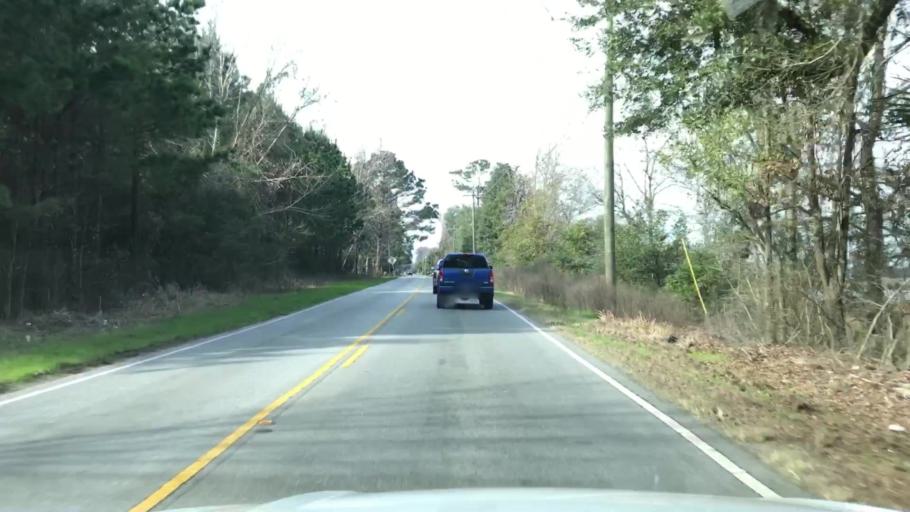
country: US
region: South Carolina
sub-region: Charleston County
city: Shell Point
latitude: 32.7777
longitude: -80.0937
